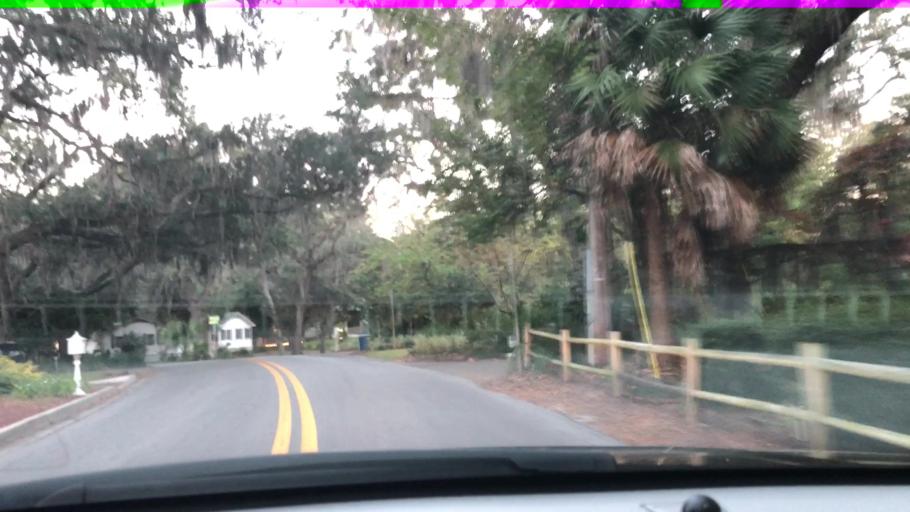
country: US
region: Florida
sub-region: Bay County
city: Panama City
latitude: 30.1351
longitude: -85.6415
